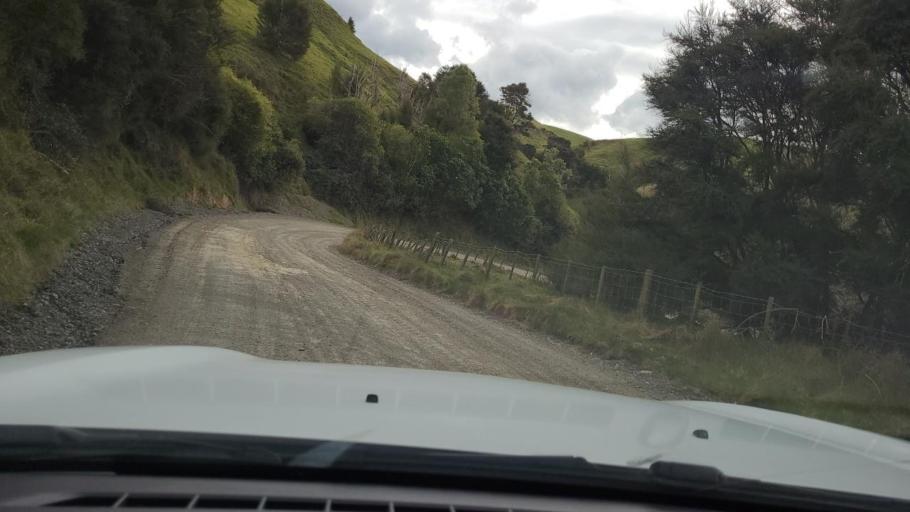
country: NZ
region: Hawke's Bay
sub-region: Napier City
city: Napier
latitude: -39.3015
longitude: 176.8291
